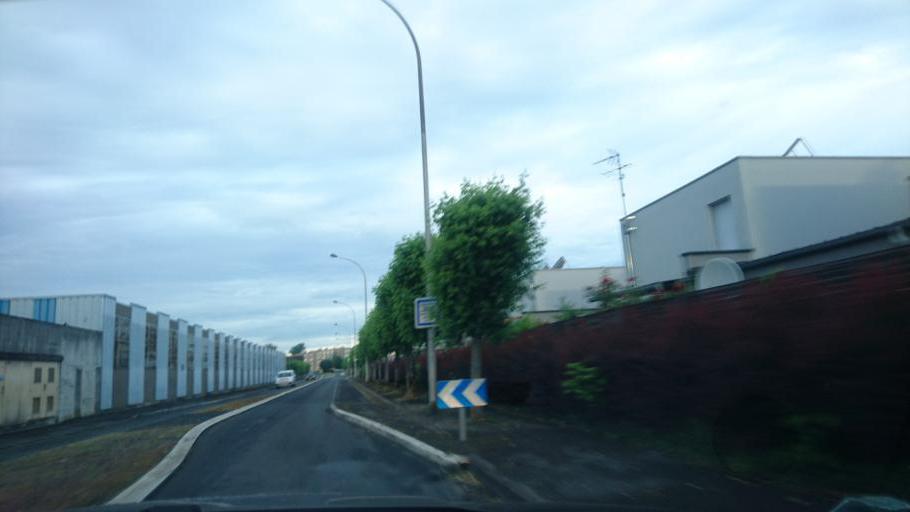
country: FR
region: Limousin
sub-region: Departement de la Correze
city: Brive-la-Gaillarde
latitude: 45.1550
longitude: 1.5004
